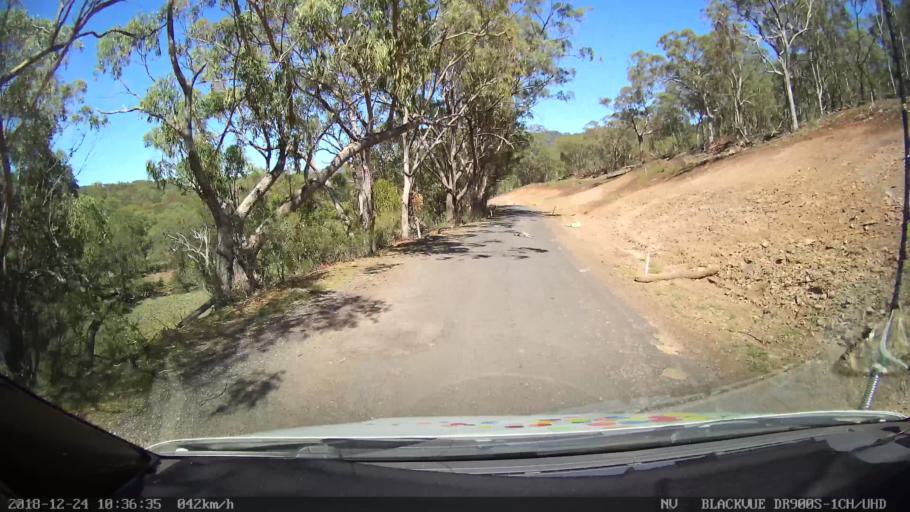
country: AU
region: New South Wales
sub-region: Upper Hunter Shire
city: Merriwa
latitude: -31.8449
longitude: 150.4990
